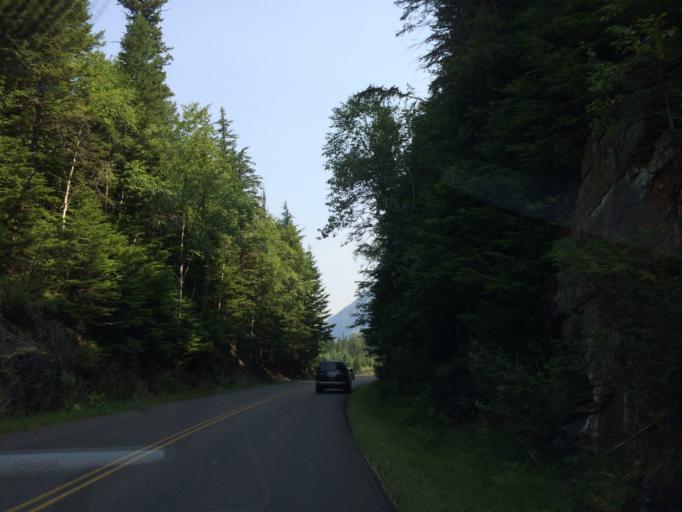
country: US
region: Montana
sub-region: Flathead County
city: Columbia Falls
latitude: 48.6442
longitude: -113.8491
